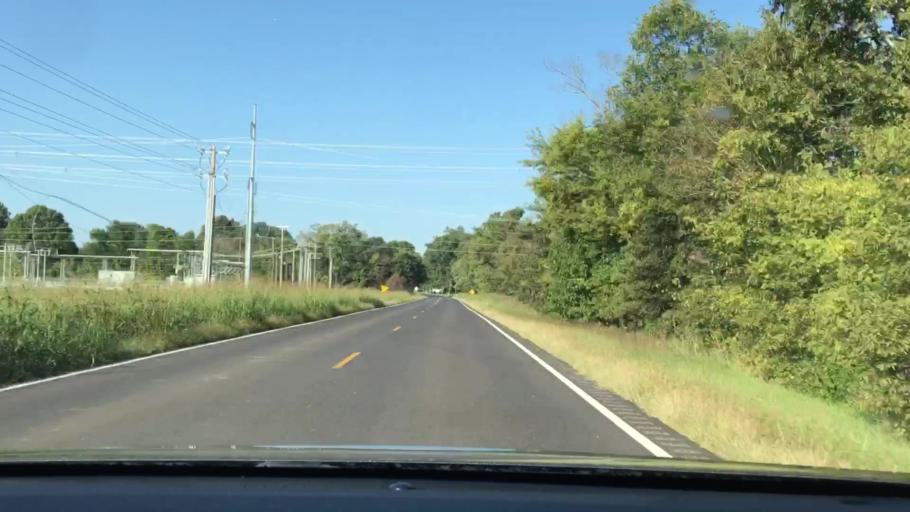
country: US
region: Kentucky
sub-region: Marshall County
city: Benton
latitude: 36.7685
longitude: -88.2893
